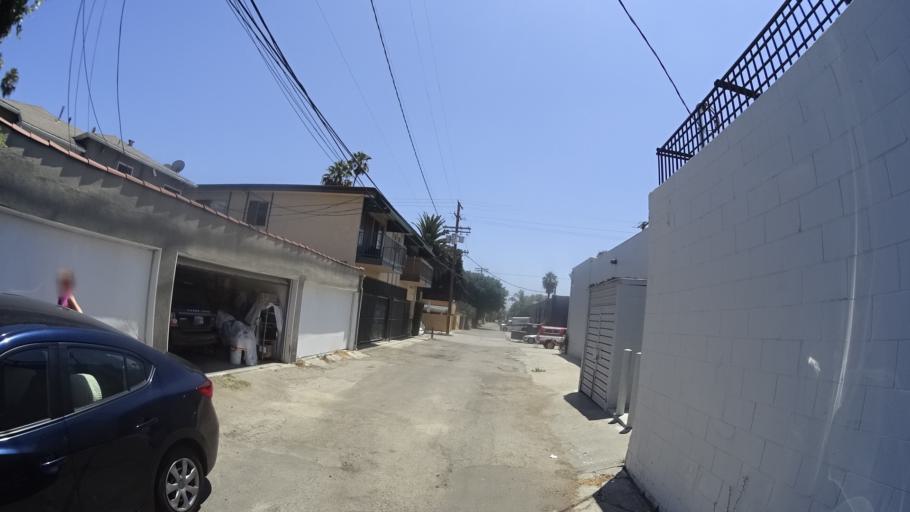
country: US
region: California
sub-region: Los Angeles County
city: Hollywood
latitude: 34.0857
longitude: -118.3381
